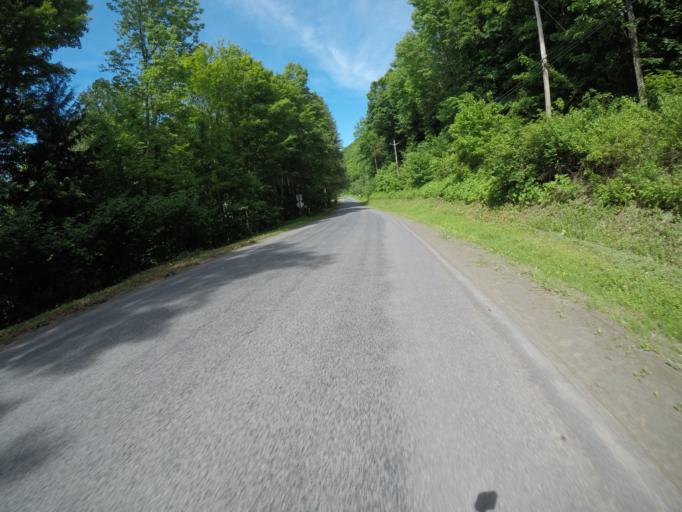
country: US
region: New York
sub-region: Delaware County
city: Stamford
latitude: 42.1361
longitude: -74.6524
